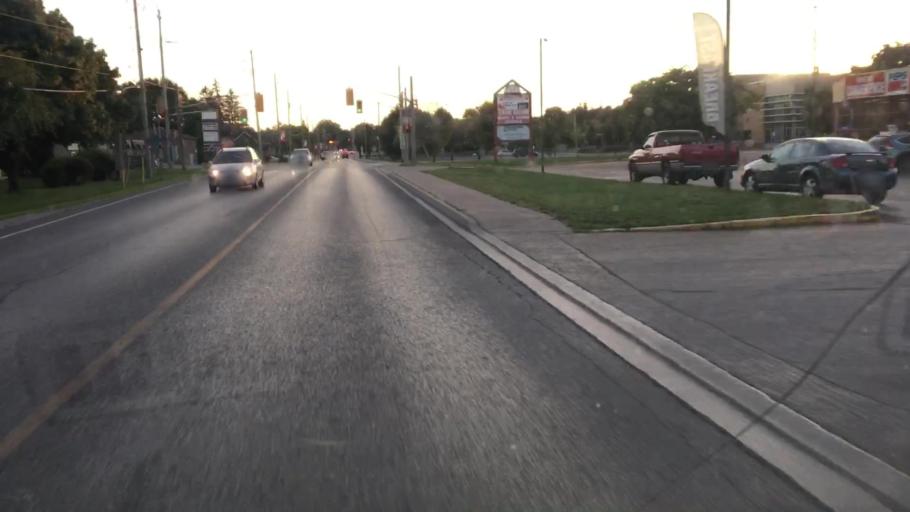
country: CA
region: Ontario
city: Quinte West
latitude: 44.0436
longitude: -77.7284
